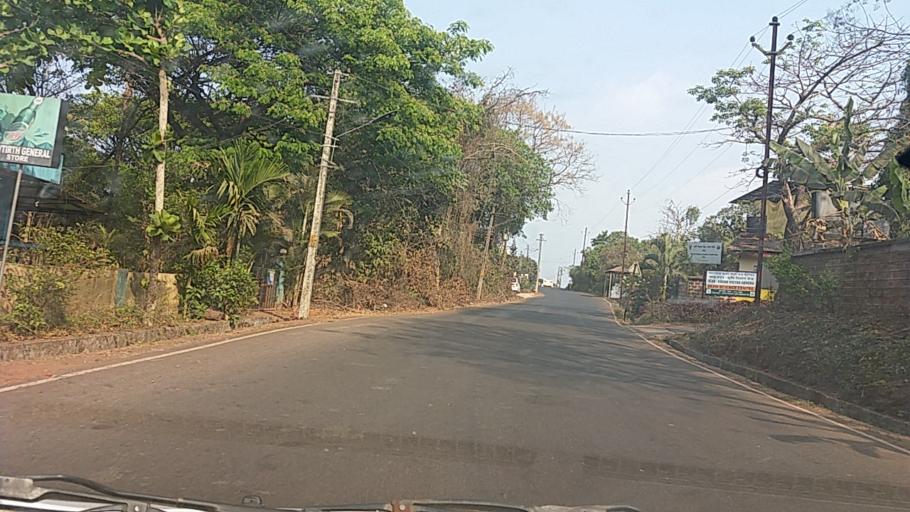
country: IN
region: Goa
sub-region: North Goa
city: Jua
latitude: 15.4935
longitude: 73.9198
